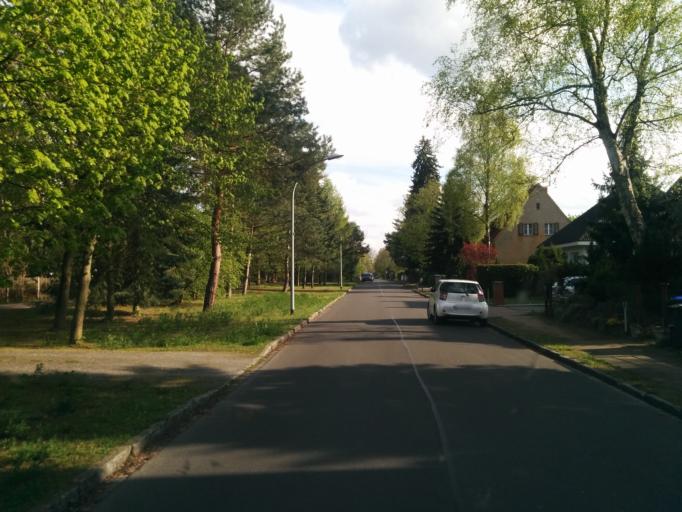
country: DE
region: Brandenburg
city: Kleinmachnow
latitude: 52.4070
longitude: 13.2051
